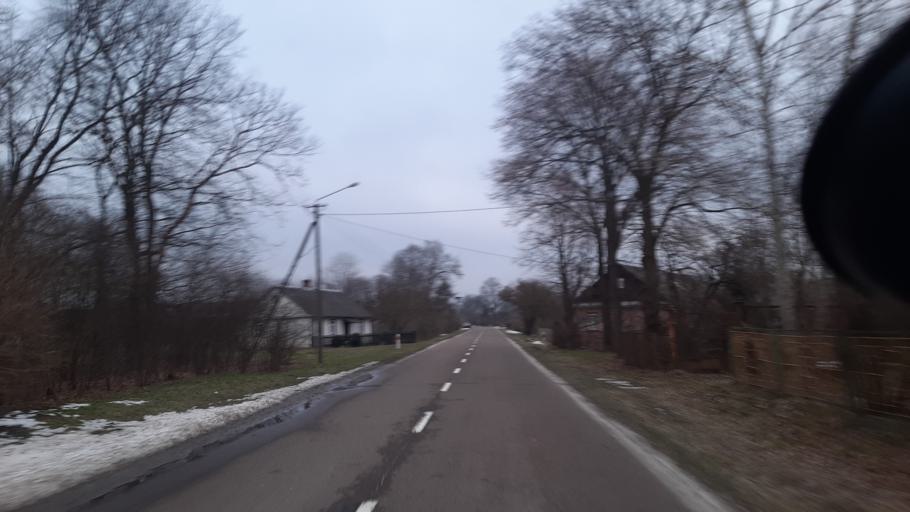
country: PL
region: Lublin Voivodeship
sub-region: Powiat parczewski
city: Podedworze
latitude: 51.5919
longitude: 23.1931
